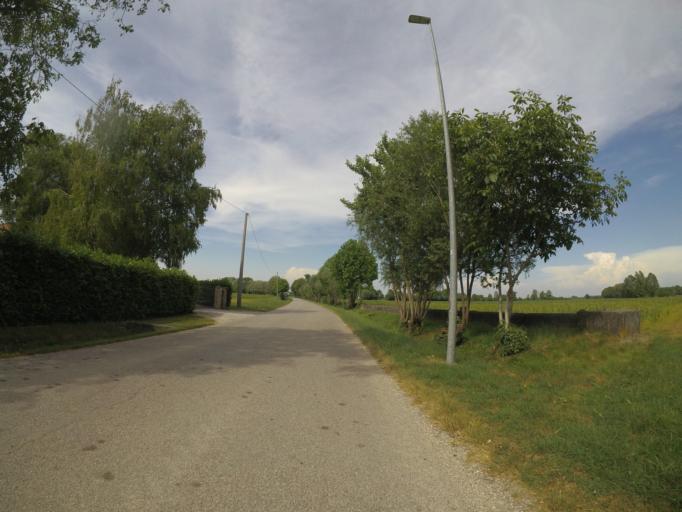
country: IT
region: Friuli Venezia Giulia
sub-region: Provincia di Udine
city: Camino al Tagliamento
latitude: 45.9430
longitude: 12.9385
